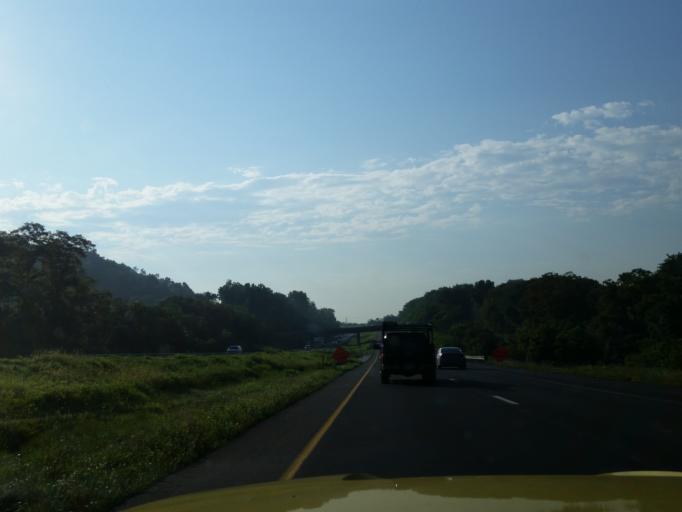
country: US
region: Pennsylvania
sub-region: Lancaster County
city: Columbia
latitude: 40.0434
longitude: -76.4856
